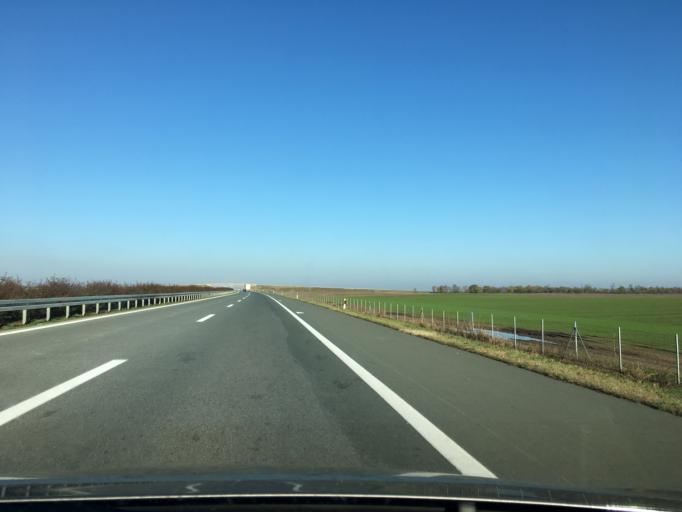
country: RS
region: Autonomna Pokrajina Vojvodina
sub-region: Severnobacki Okrug
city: Mali Igos
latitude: 45.6910
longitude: 19.7255
